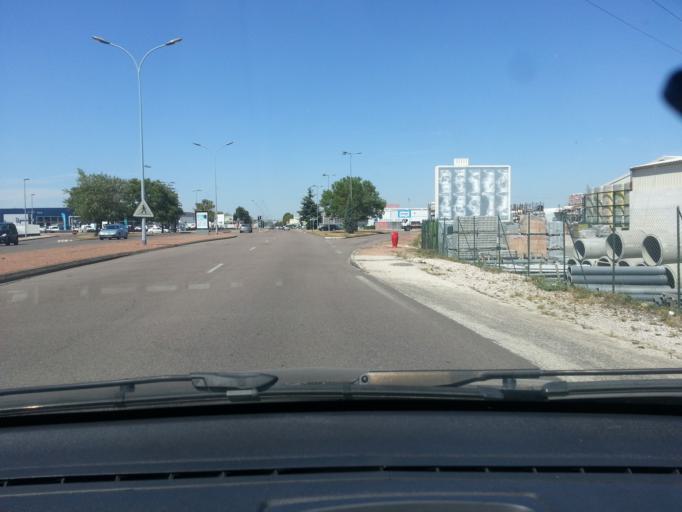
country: FR
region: Bourgogne
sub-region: Departement de la Cote-d'Or
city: Chenove
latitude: 47.2899
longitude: 5.0203
